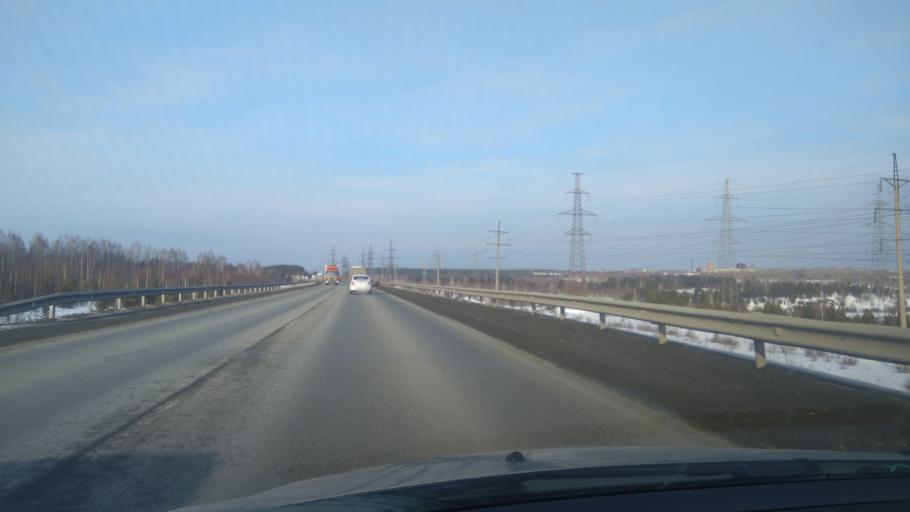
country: RU
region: Sverdlovsk
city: Revda
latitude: 56.8279
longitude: 59.9489
